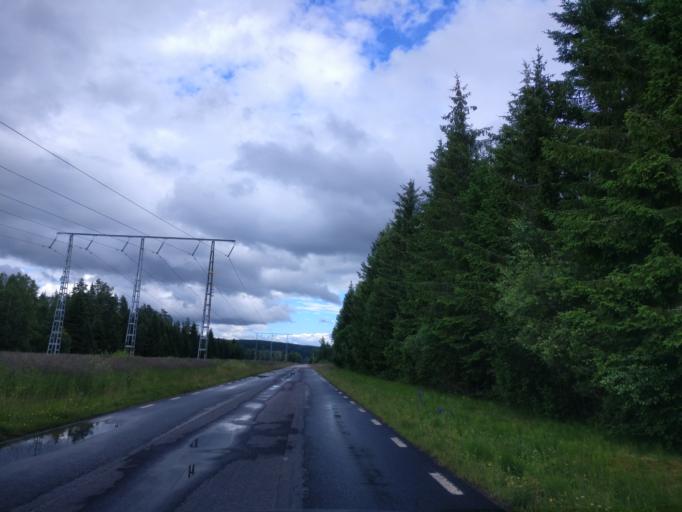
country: SE
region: Vaermland
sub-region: Hagfors Kommun
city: Hagfors
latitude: 60.0345
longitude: 13.5652
